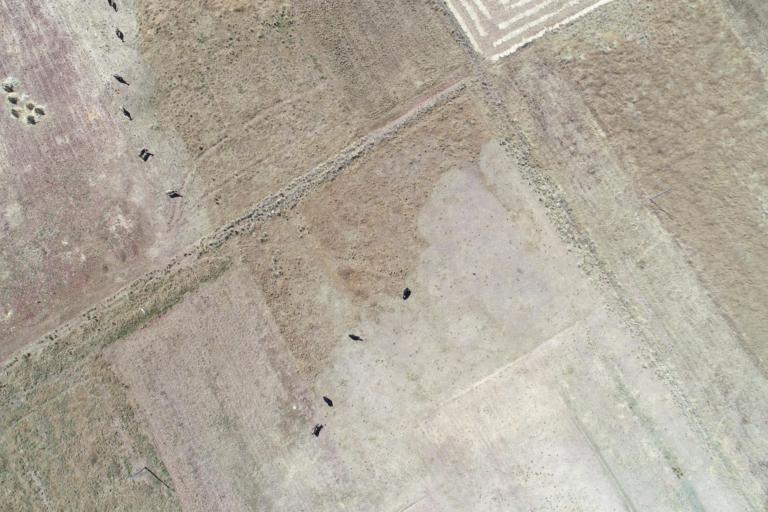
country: BO
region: La Paz
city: Tiahuanaco
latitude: -16.5958
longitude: -68.7759
